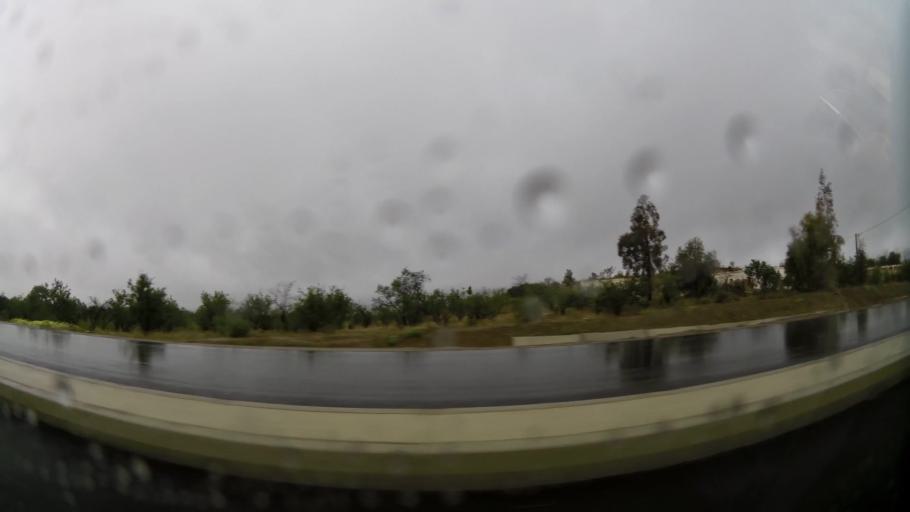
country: MA
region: Oriental
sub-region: Nador
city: Midar
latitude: 34.8574
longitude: -3.7221
